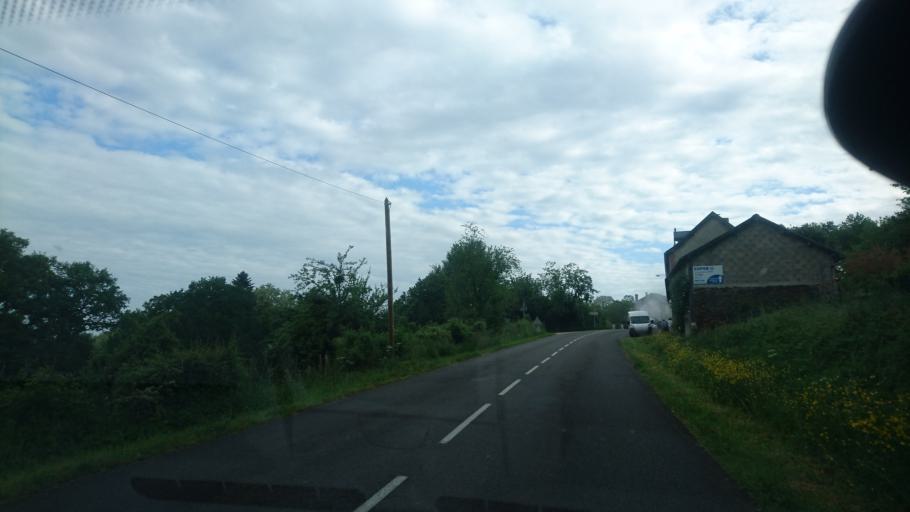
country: FR
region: Limousin
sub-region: Departement de la Haute-Vienne
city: Saint-Germain-les-Belles
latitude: 45.6061
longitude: 1.4822
